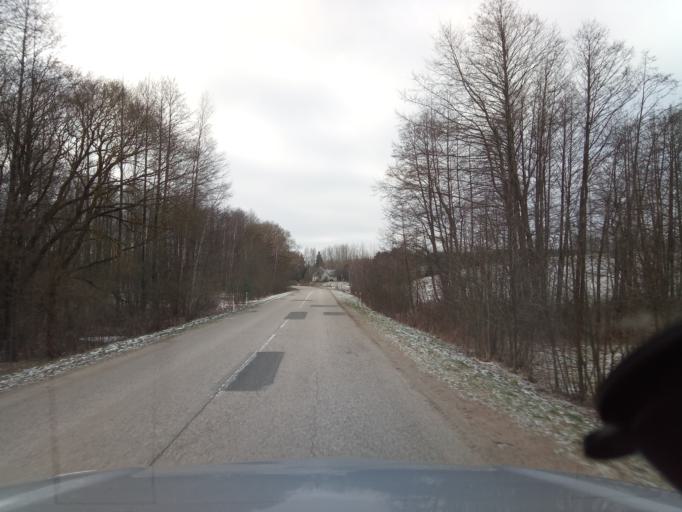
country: LT
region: Alytaus apskritis
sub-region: Alytaus rajonas
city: Daugai
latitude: 54.3460
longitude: 24.3142
